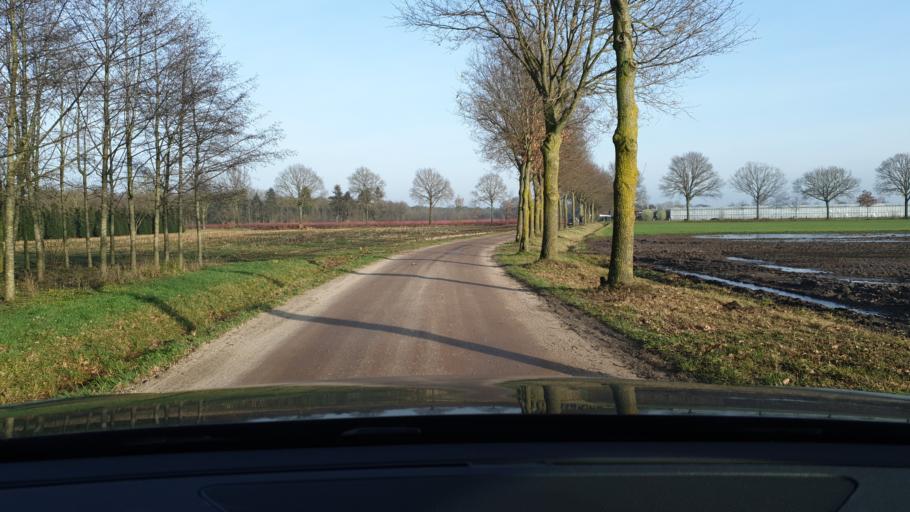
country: NL
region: Limburg
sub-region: Gemeente Peel en Maas
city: Maasbree
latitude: 51.4288
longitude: 6.0627
